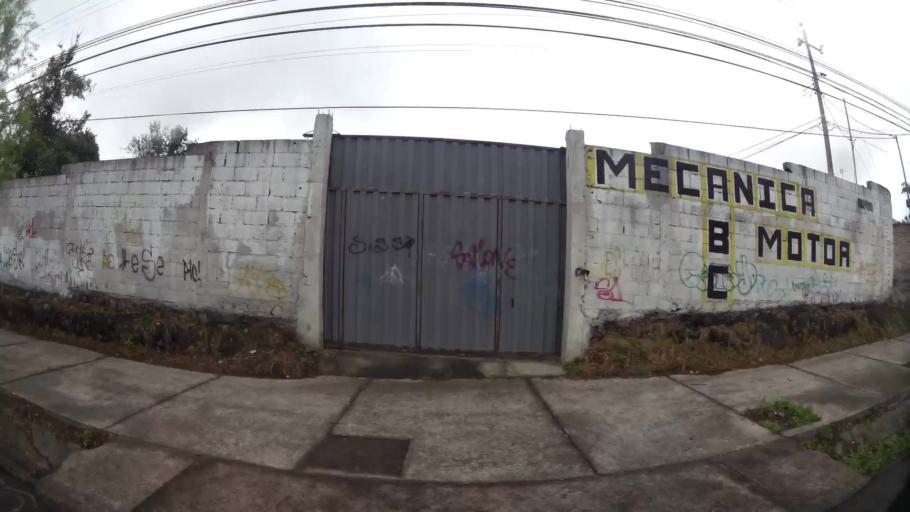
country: EC
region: Pichincha
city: Sangolqui
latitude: -0.2802
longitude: -78.4619
